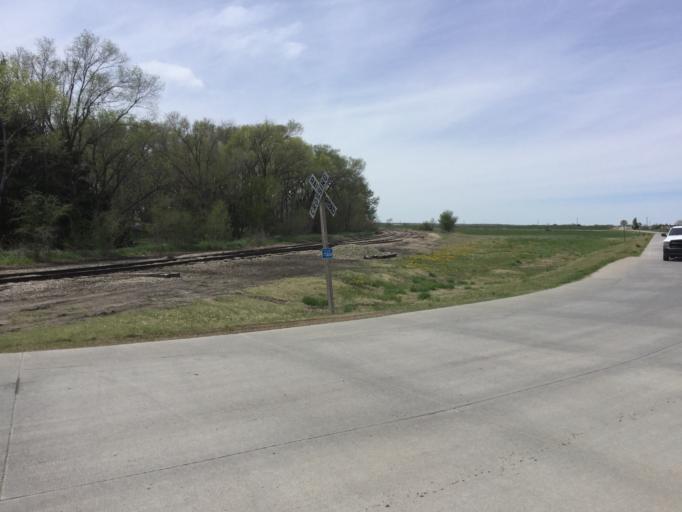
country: US
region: Kansas
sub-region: Osborne County
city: Osborne
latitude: 39.5021
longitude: -98.5470
